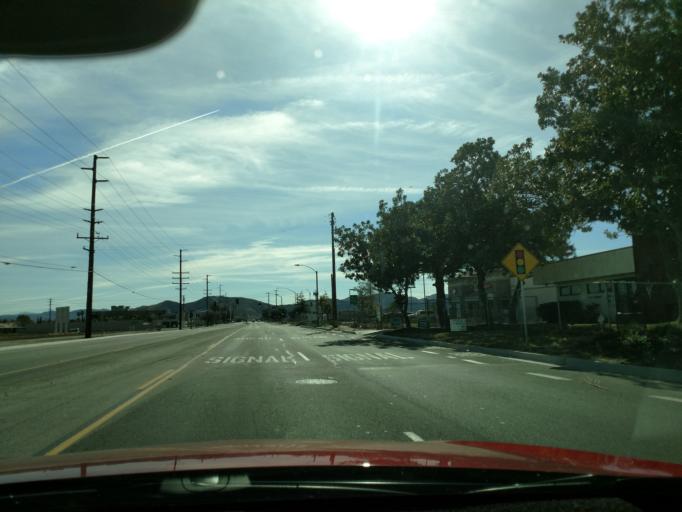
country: US
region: California
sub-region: Riverside County
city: Hemet
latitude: 33.7373
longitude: -117.0067
